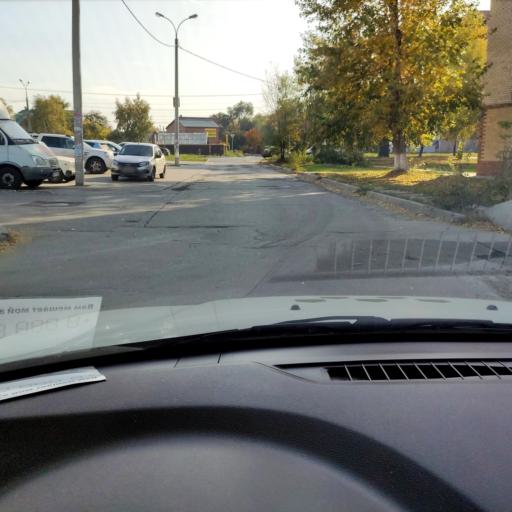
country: RU
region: Samara
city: Tol'yatti
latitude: 53.5303
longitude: 49.4025
